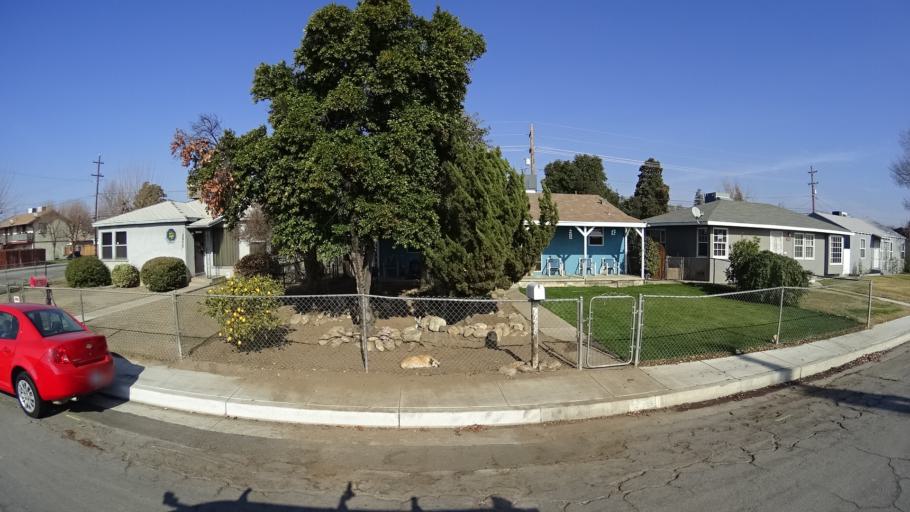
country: US
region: California
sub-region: Kern County
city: Bakersfield
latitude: 35.3724
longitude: -119.0359
